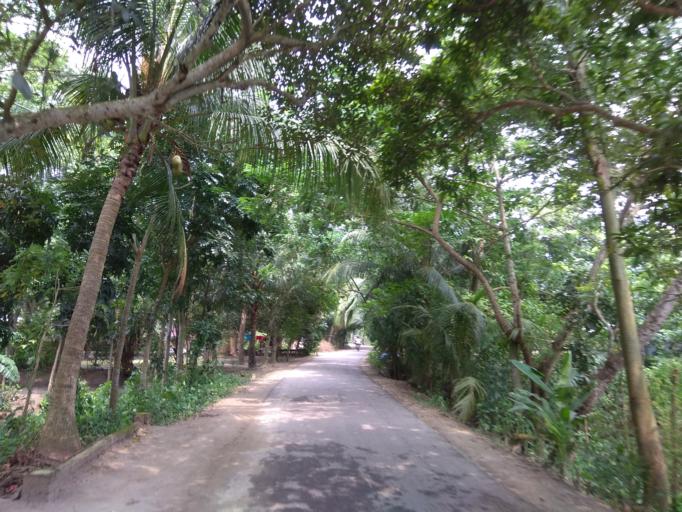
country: BD
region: Dhaka
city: Dohar
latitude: 23.4994
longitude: 90.0101
